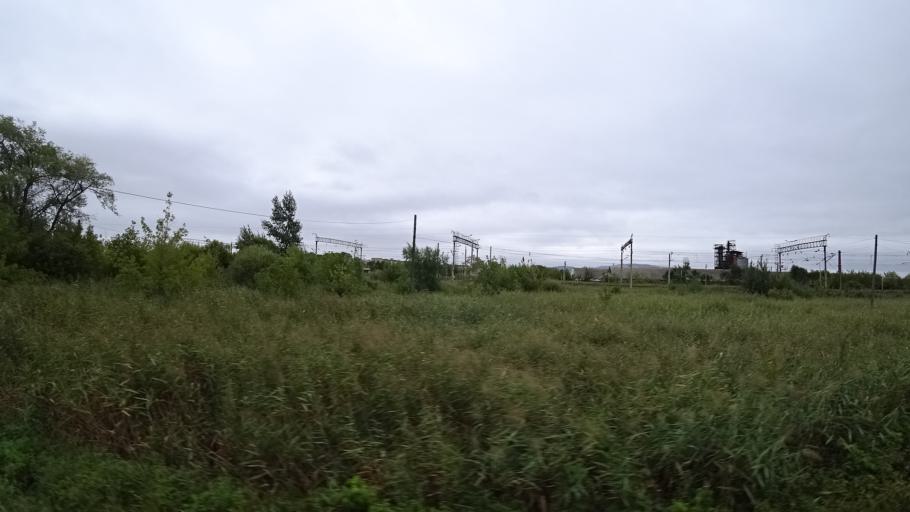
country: RU
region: Primorskiy
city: Chernigovka
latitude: 44.3365
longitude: 132.5264
